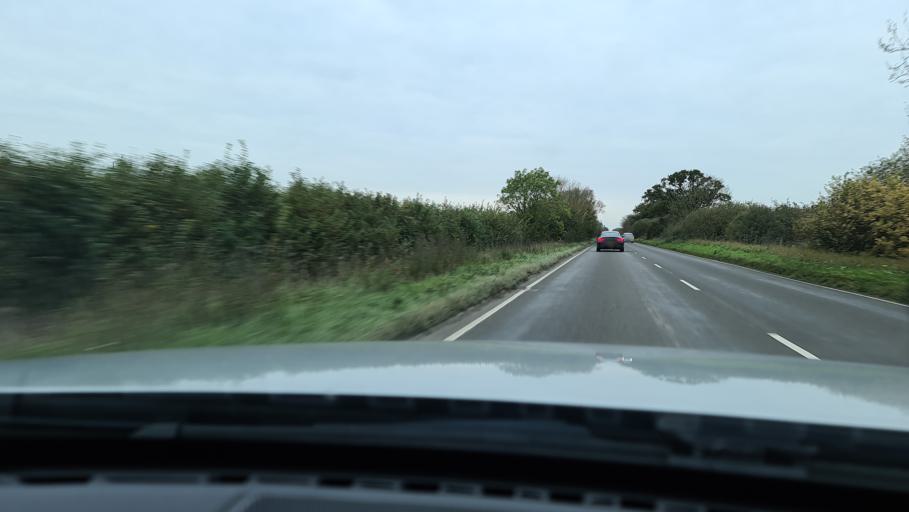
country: GB
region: England
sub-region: Buckinghamshire
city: Steeple Claydon
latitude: 51.8715
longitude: -1.0354
